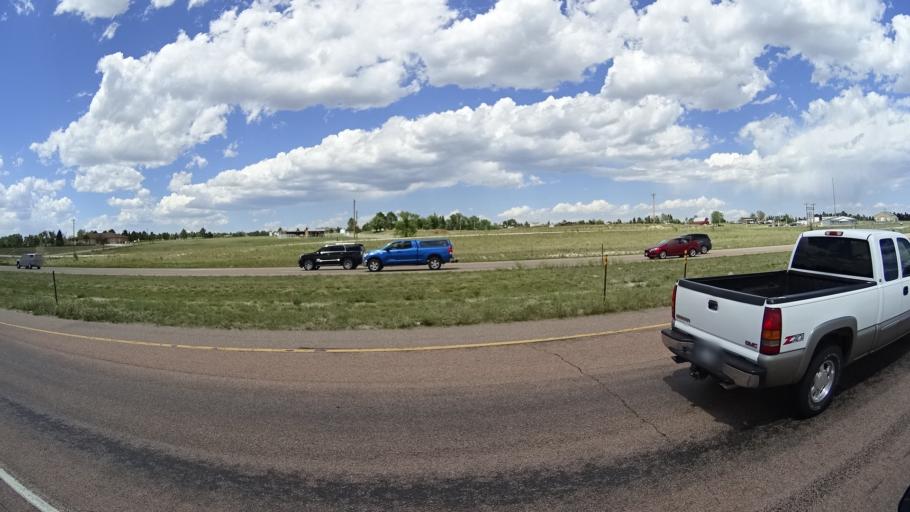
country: US
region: Colorado
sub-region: El Paso County
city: Black Forest
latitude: 38.9404
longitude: -104.6663
